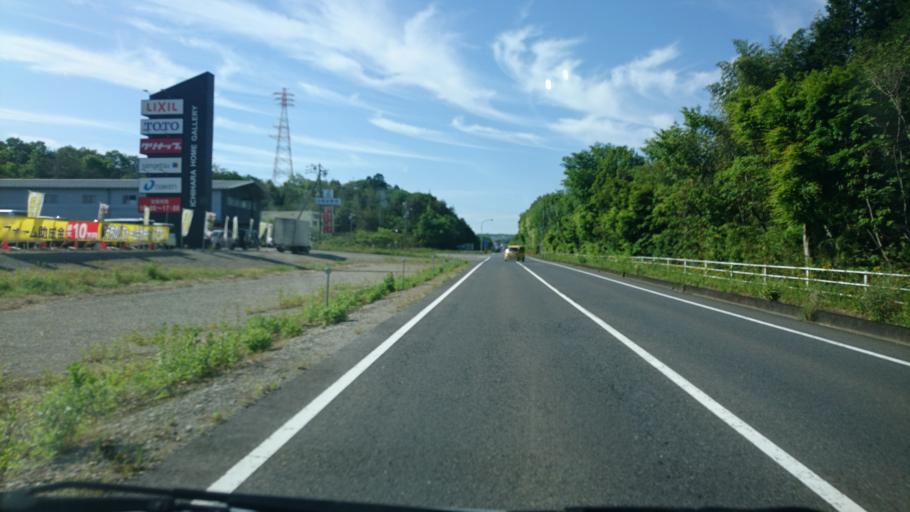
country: JP
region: Gifu
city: Minokamo
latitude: 35.4048
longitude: 137.0439
